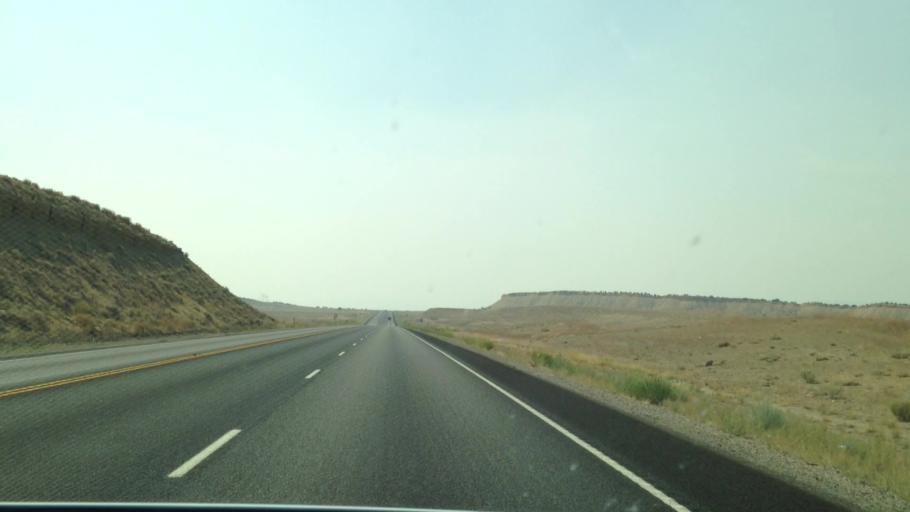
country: US
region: Utah
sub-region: Carbon County
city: Wellington
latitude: 39.5391
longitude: -110.6080
